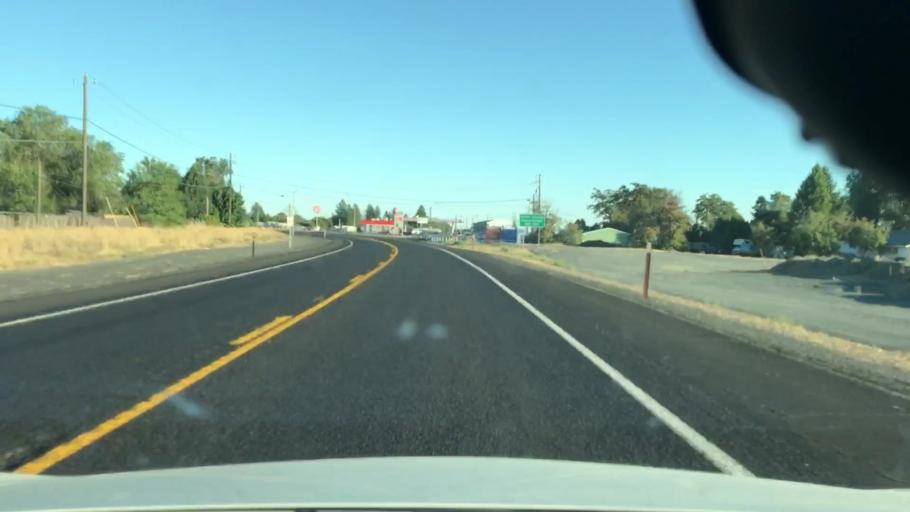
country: US
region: Washington
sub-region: Grant County
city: Cascade Valley
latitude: 47.1635
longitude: -119.3252
